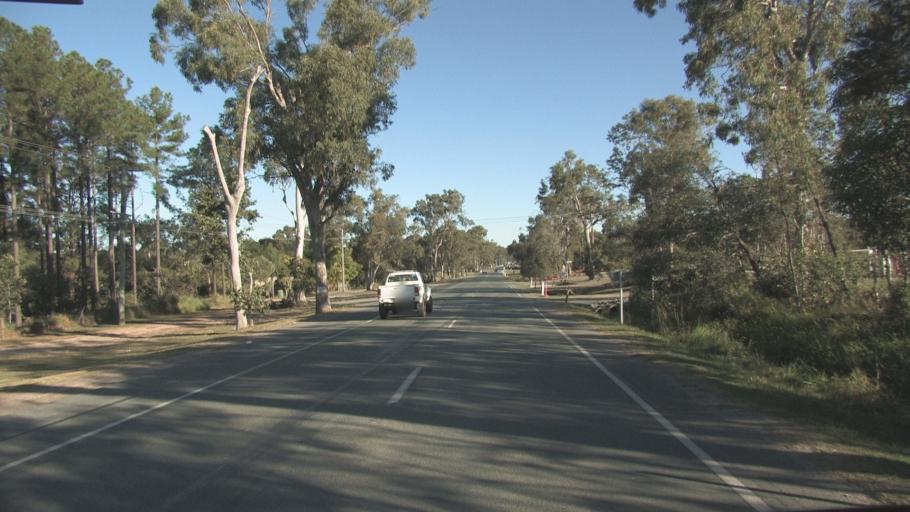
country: AU
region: Queensland
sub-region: Logan
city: Logan Reserve
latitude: -27.7125
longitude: 153.0931
